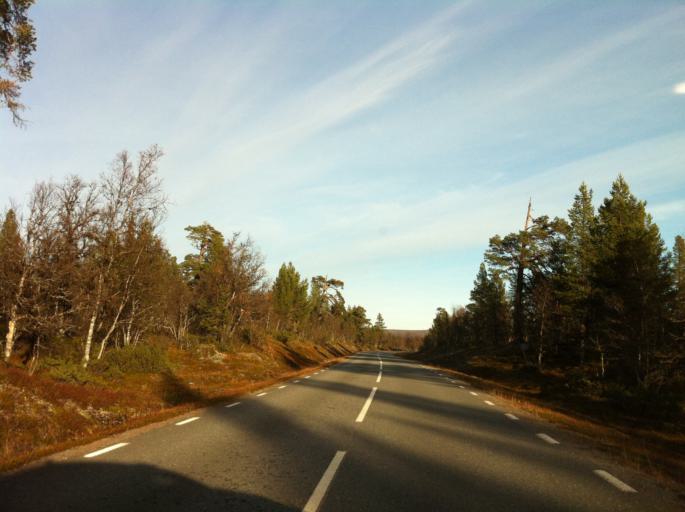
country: NO
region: Hedmark
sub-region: Engerdal
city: Engerdal
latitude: 62.0754
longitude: 12.1790
